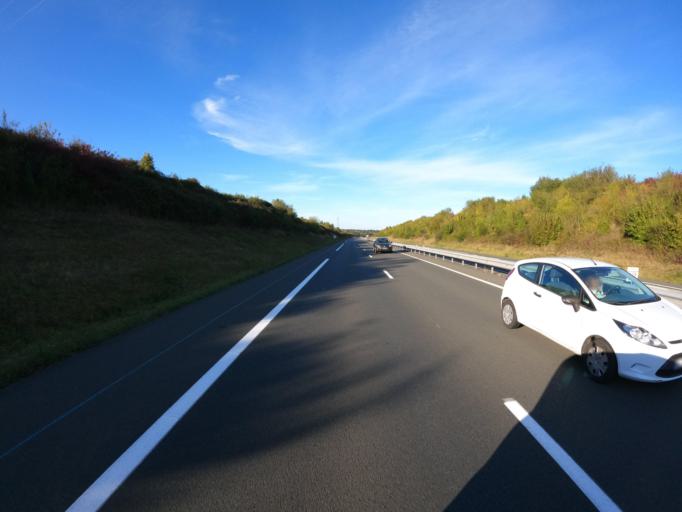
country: FR
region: Pays de la Loire
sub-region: Departement de Maine-et-Loire
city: Chemille-Melay
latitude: 47.2161
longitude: -0.7629
